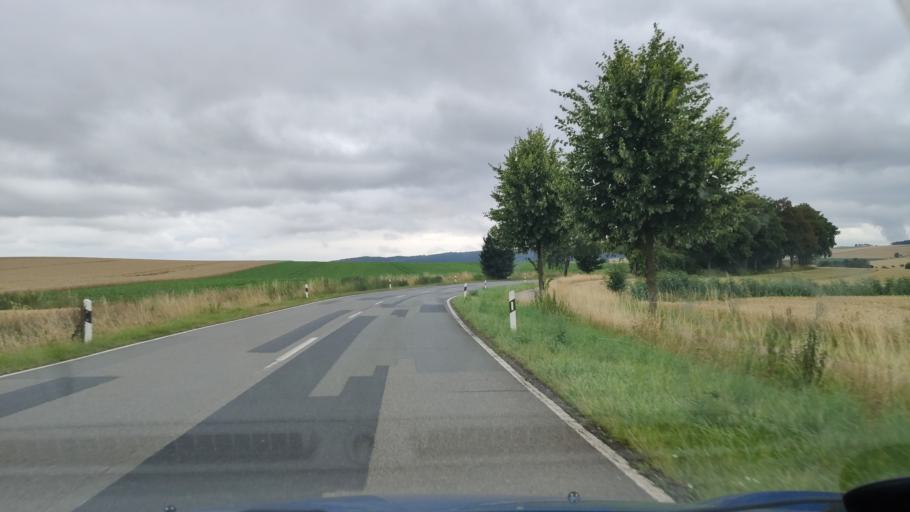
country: DE
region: Lower Saxony
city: Coppenbrugge
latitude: 52.0990
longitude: 9.4974
